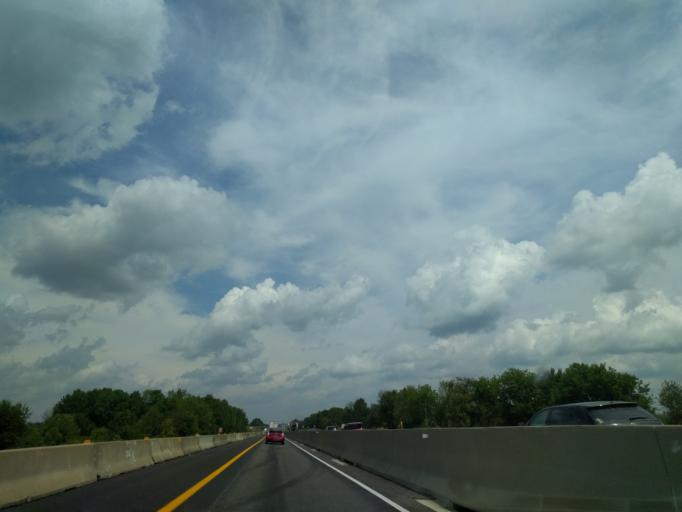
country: US
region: Kentucky
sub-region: Hardin County
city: Elizabethtown
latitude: 37.5634
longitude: -85.8759
